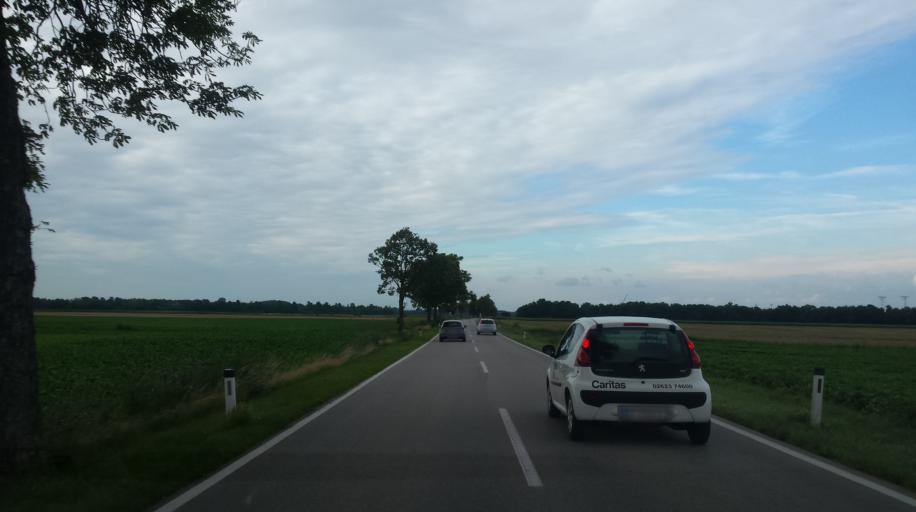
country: AT
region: Lower Austria
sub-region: Politischer Bezirk Baden
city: Mitterndorf an der Fischa
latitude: 47.9871
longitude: 16.4387
